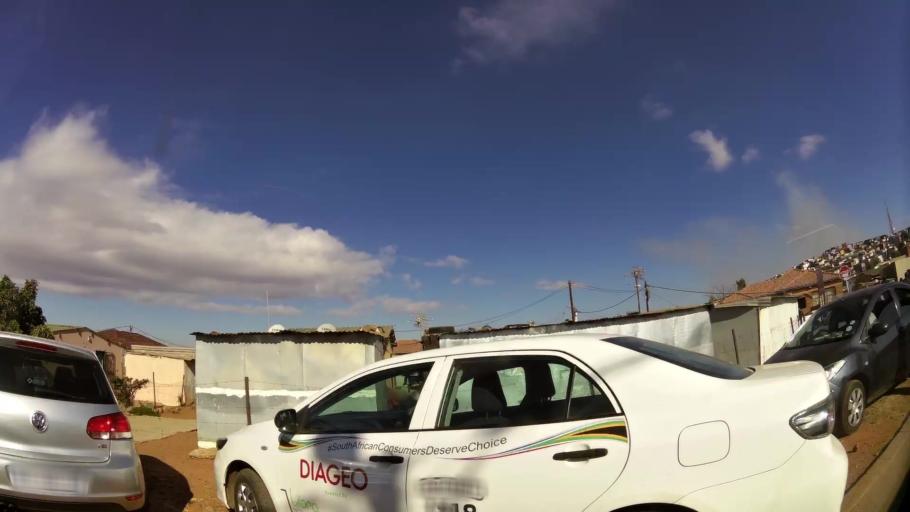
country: ZA
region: Gauteng
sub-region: City of Tshwane Metropolitan Municipality
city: Cullinan
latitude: -25.6950
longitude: 28.4169
